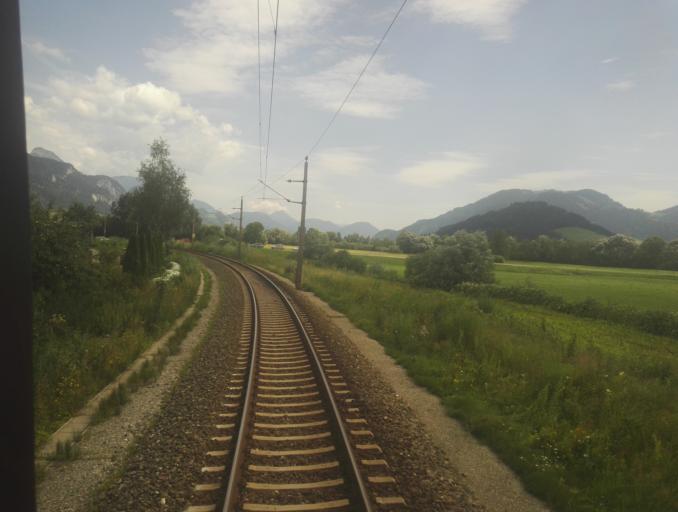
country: AT
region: Styria
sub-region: Politischer Bezirk Liezen
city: Irdning
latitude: 47.5176
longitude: 14.0833
